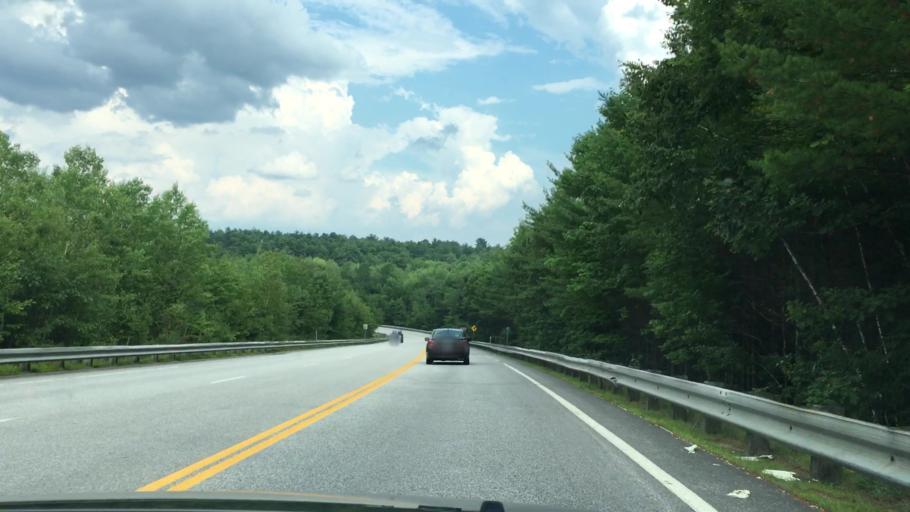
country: US
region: New Hampshire
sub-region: Belknap County
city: Gilford
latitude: 43.5727
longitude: -71.3579
